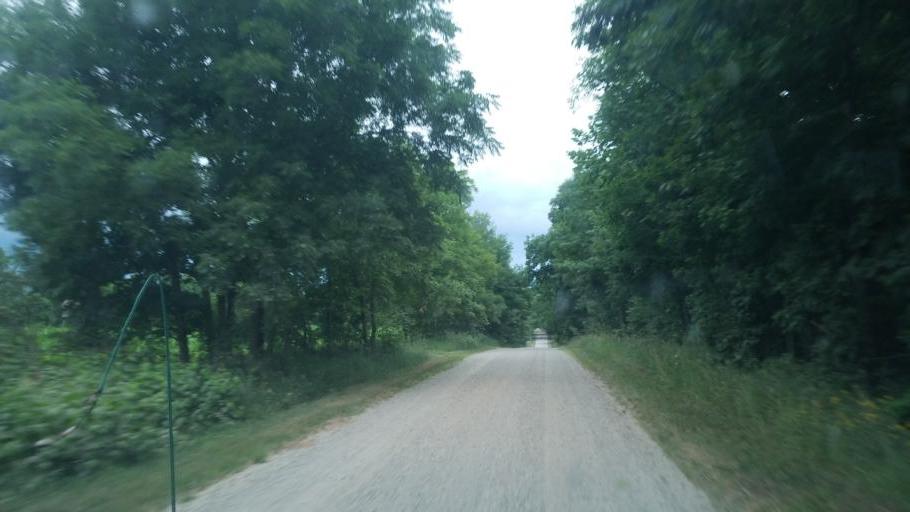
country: US
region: Ohio
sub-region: Defiance County
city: Hicksville
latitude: 41.3288
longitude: -84.8229
